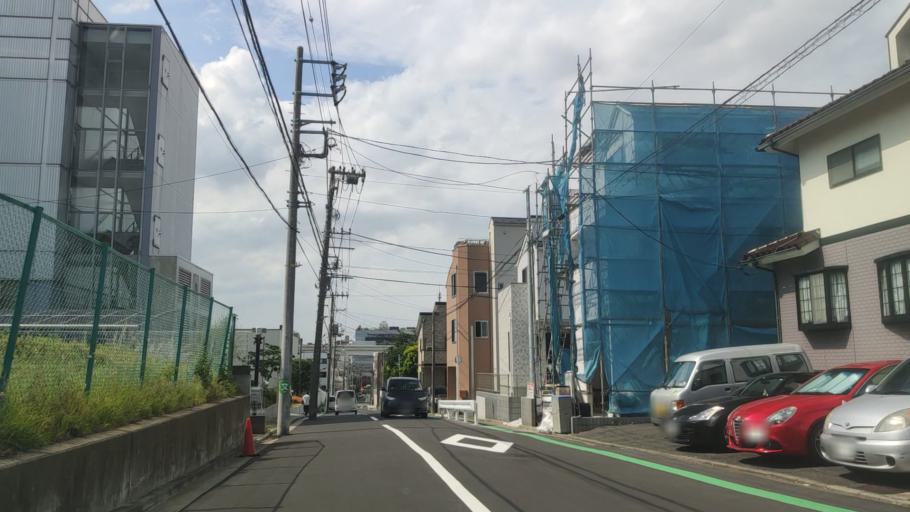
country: JP
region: Kanagawa
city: Yokohama
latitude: 35.4310
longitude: 139.6289
